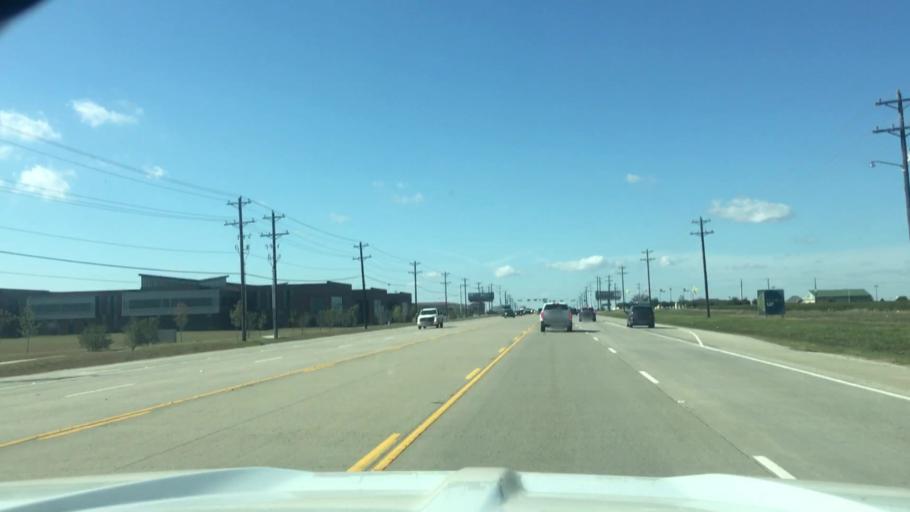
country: US
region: Texas
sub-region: Denton County
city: Little Elm
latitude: 33.2206
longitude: -96.9255
